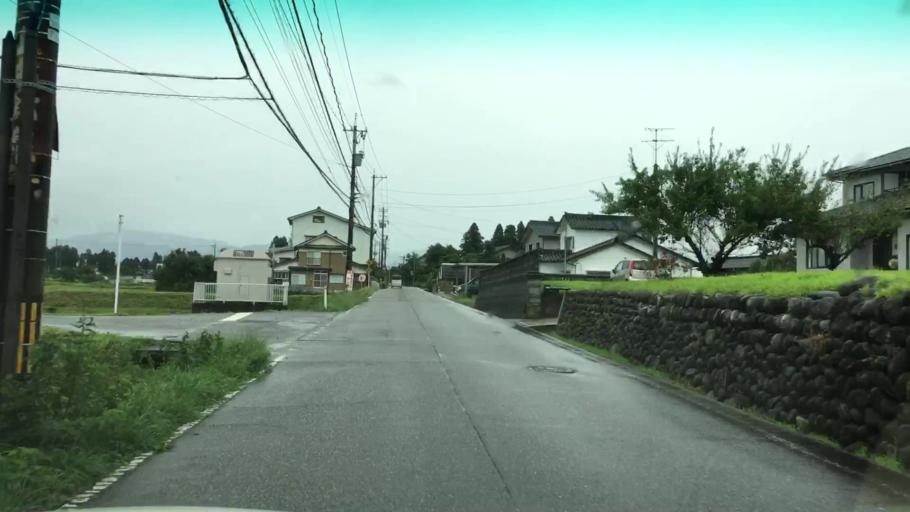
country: JP
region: Toyama
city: Kamiichi
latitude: 36.6384
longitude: 137.3200
